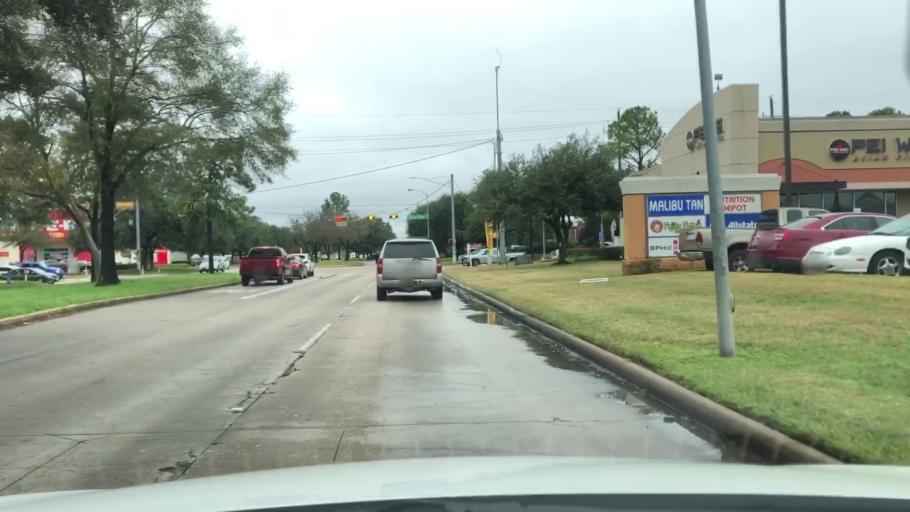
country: US
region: Texas
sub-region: Fort Bend County
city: Cinco Ranch
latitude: 29.7594
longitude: -95.7517
